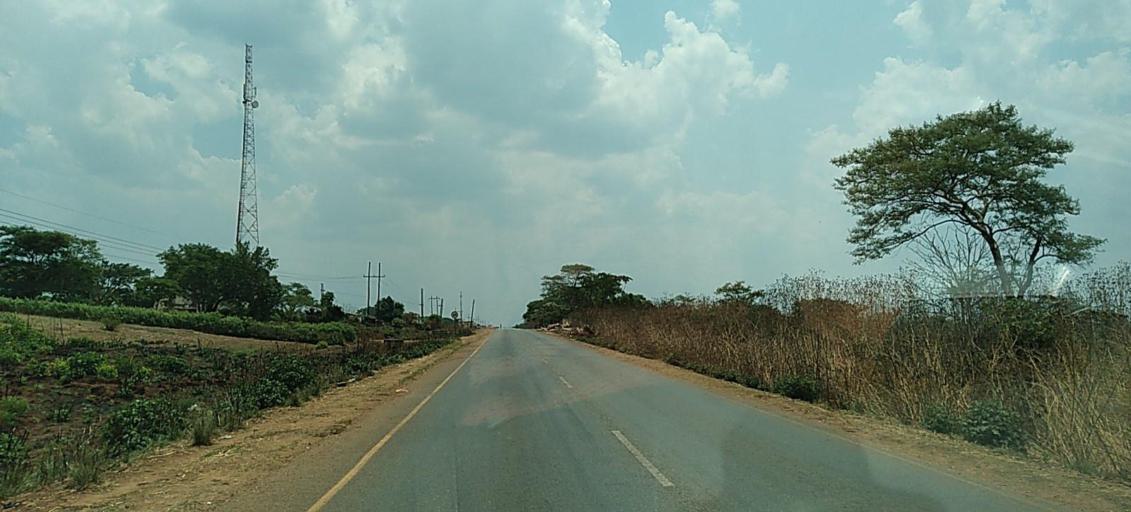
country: ZM
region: Copperbelt
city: Kalulushi
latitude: -12.8388
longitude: 27.9905
